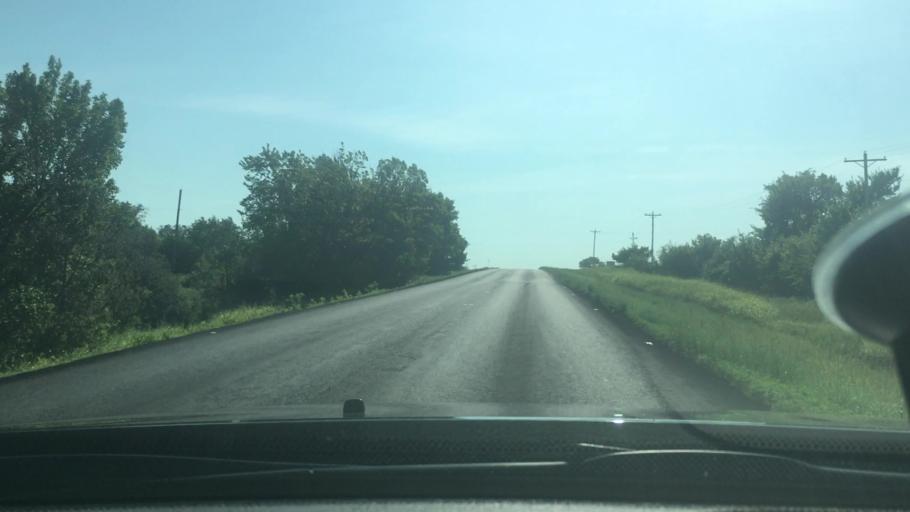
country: US
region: Oklahoma
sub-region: Garvin County
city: Pauls Valley
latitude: 34.6518
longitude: -97.2854
